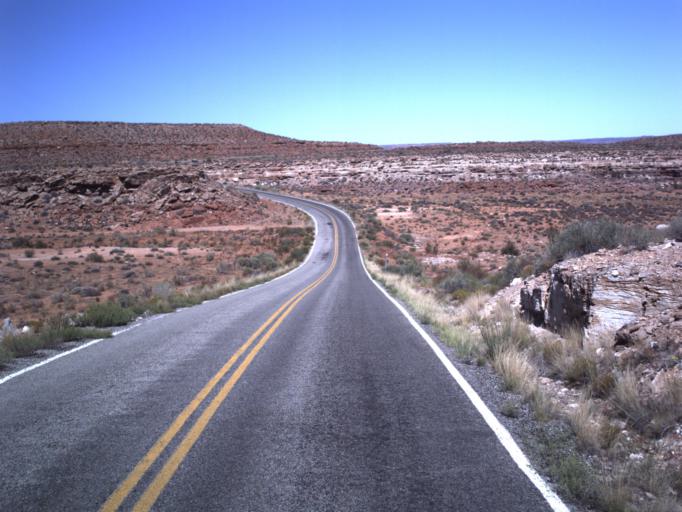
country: US
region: Arizona
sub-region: Navajo County
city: Kayenta
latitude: 37.1912
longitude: -109.9116
